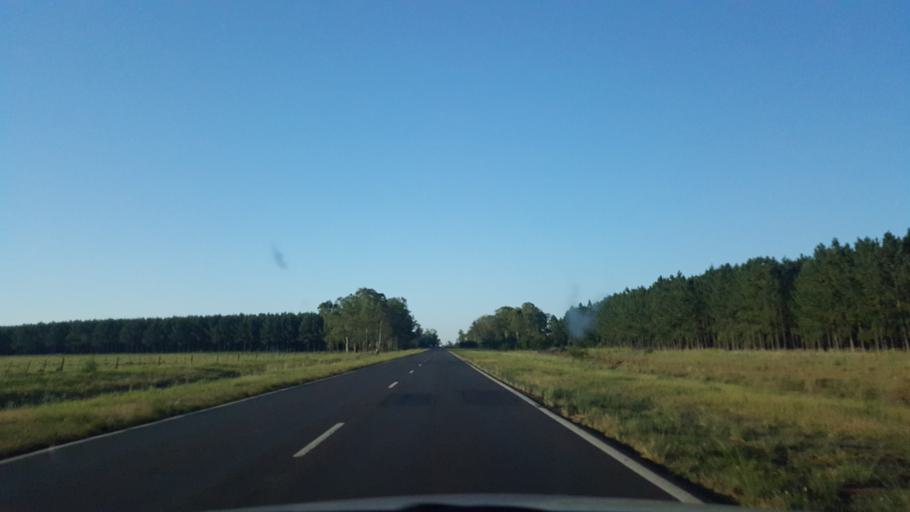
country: AR
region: Corrientes
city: Santo Tome
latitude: -28.4974
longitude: -56.1125
